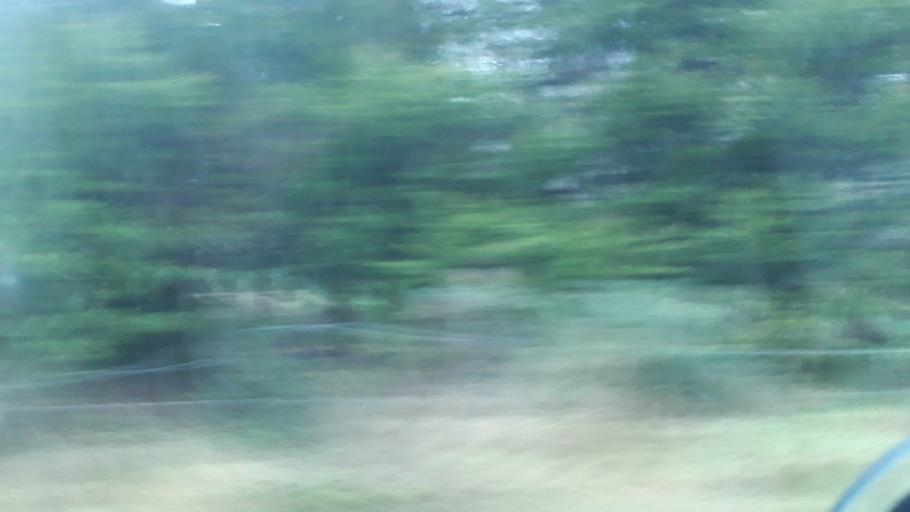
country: IE
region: Ulster
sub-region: County Donegal
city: Ramelton
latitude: 55.0764
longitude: -7.5925
